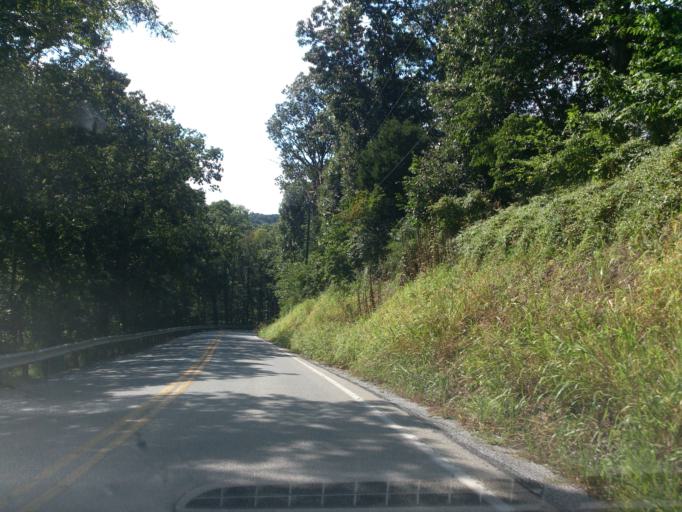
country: US
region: Pennsylvania
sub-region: York County
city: Susquehanna Trails
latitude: 39.8042
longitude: -76.4749
